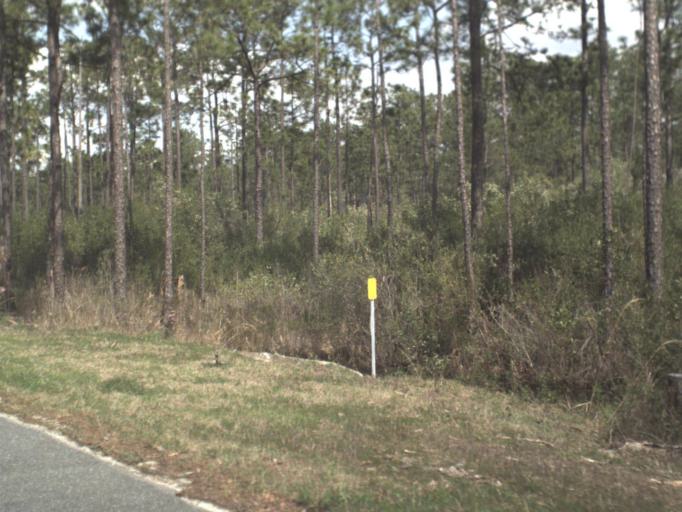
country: US
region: Florida
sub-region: Gulf County
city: Wewahitchka
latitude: 29.9895
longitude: -84.9764
